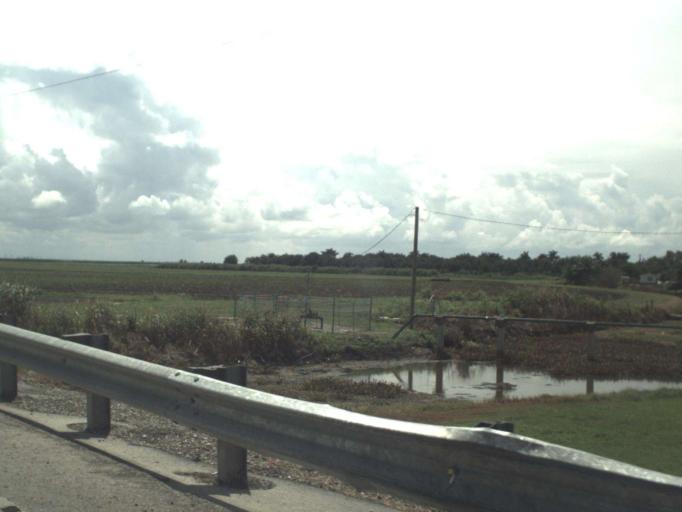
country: US
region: Florida
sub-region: Palm Beach County
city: Pahokee
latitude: 26.8138
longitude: -80.6655
